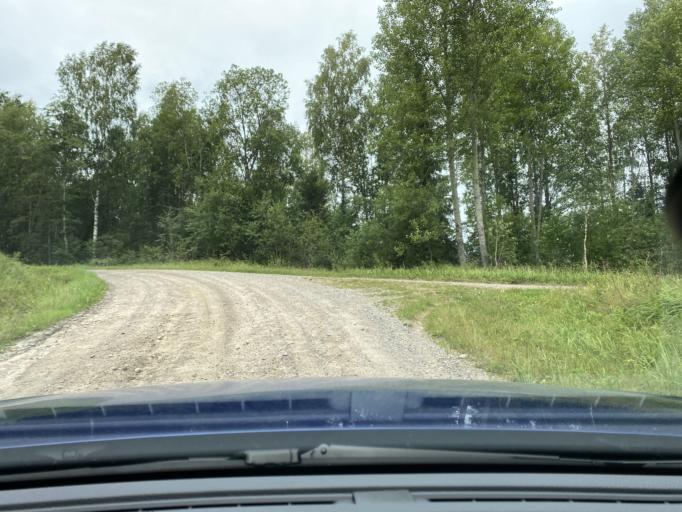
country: FI
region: Pirkanmaa
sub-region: Ylae-Pirkanmaa
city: Maenttae
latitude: 62.0227
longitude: 24.7231
